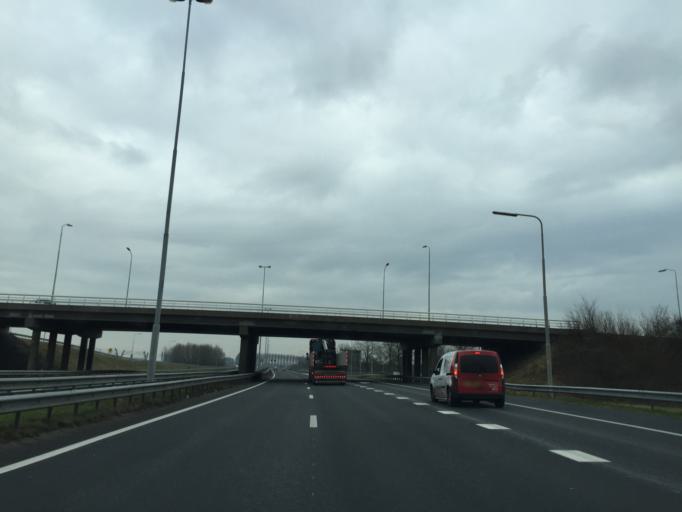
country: NL
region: North Brabant
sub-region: Gemeente Woudrichem
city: Woudrichem
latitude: 51.8436
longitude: 5.0021
